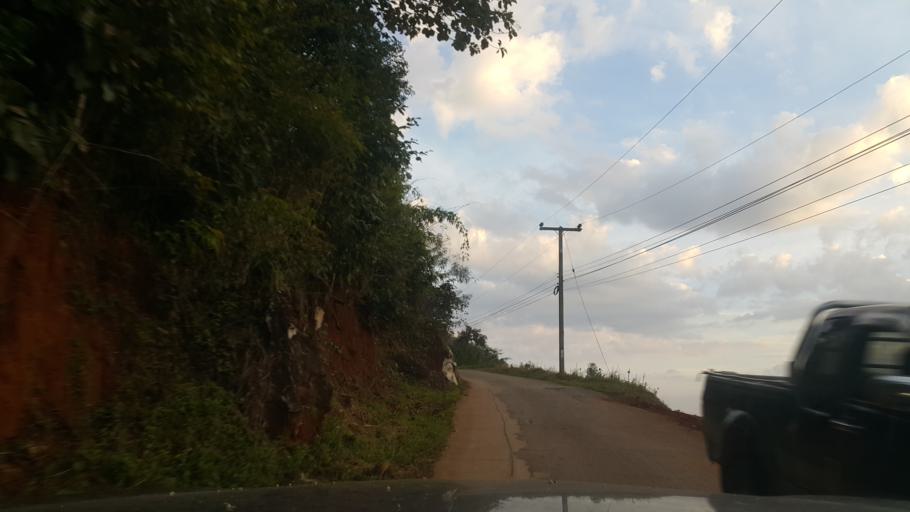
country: TH
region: Chiang Mai
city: Samoeng
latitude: 18.9754
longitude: 98.6791
